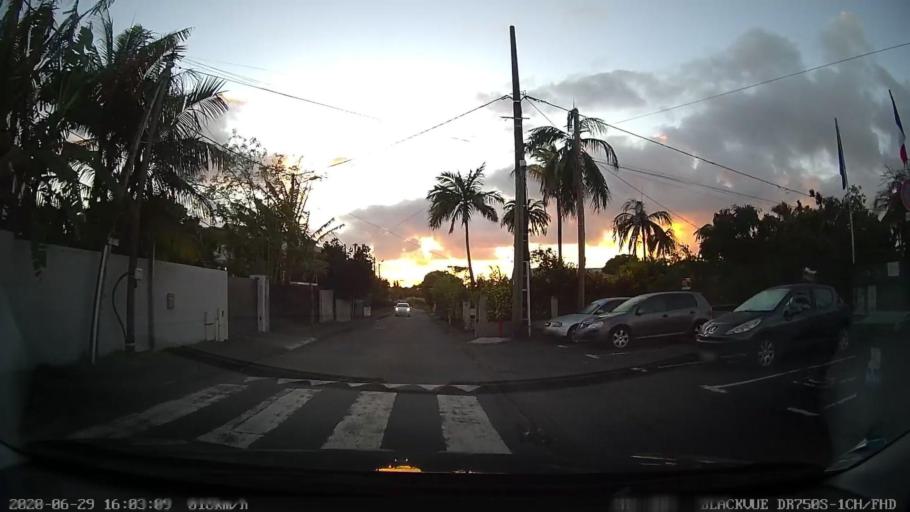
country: RE
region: Reunion
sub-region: Reunion
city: Bras-Panon
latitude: -20.9926
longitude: 55.6796
